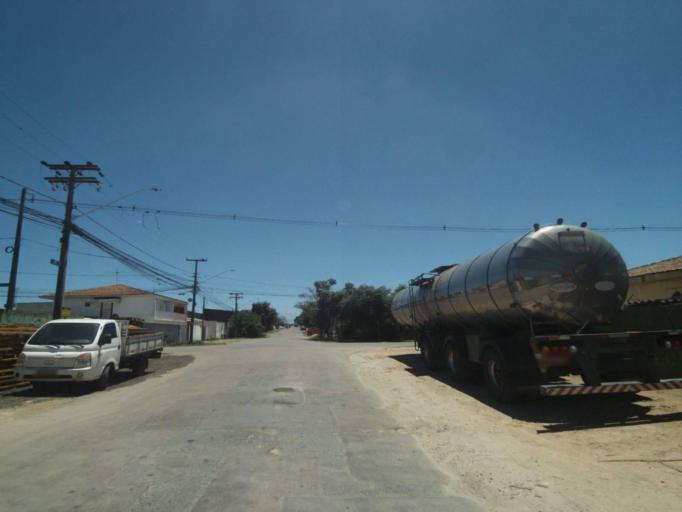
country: BR
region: Parana
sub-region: Curitiba
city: Curitiba
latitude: -25.4819
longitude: -49.3473
